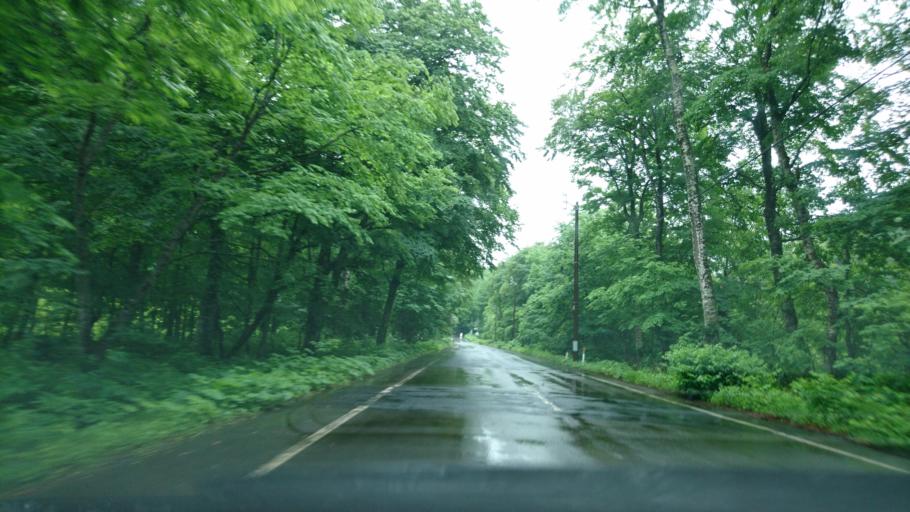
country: JP
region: Iwate
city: Ichinoseki
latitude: 39.0048
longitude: 140.8491
